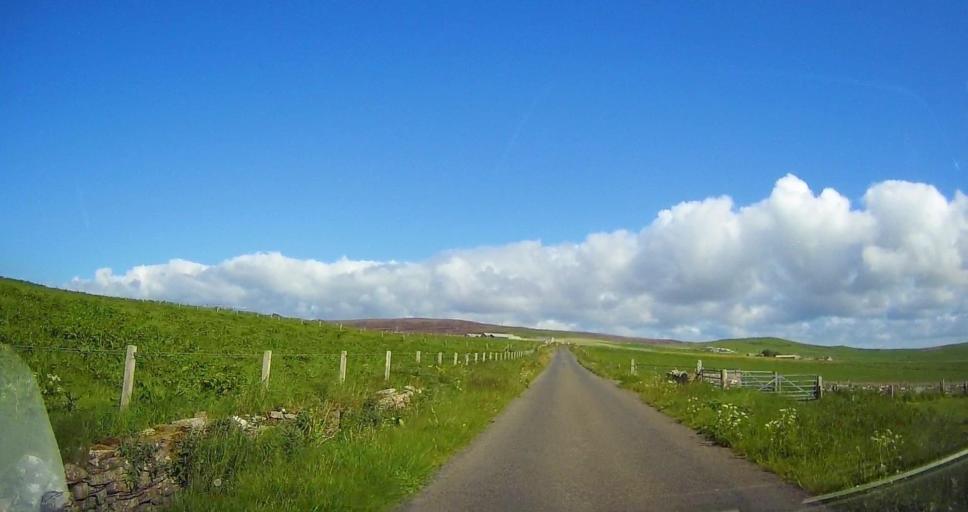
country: GB
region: Scotland
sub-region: Orkney Islands
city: Stromness
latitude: 58.9877
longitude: -3.1497
